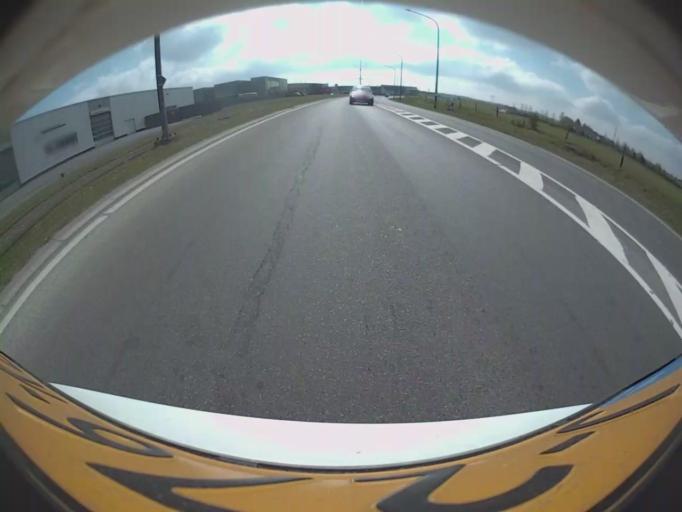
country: BE
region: Wallonia
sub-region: Province du Luxembourg
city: Marche-en-Famenne
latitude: 50.2415
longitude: 5.3361
